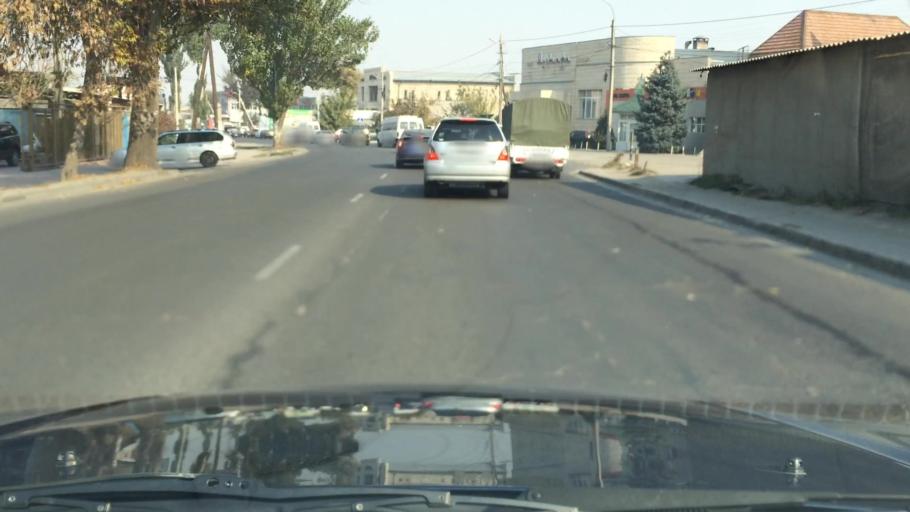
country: KG
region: Chuy
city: Lebedinovka
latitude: 42.8773
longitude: 74.6375
